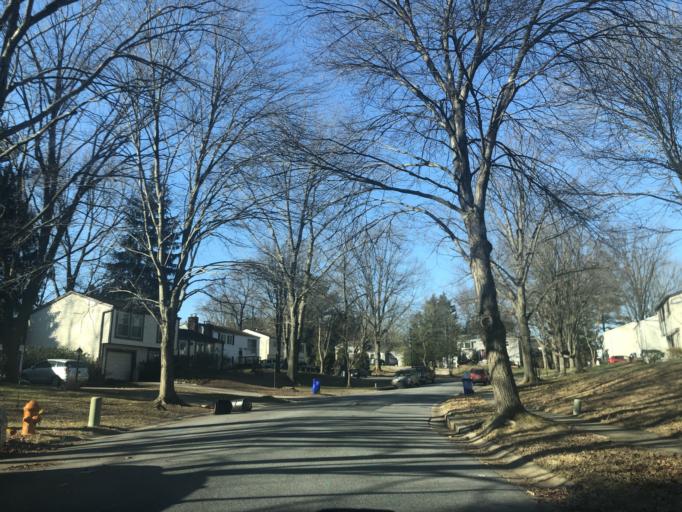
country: US
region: Maryland
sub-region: Howard County
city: Columbia
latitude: 39.2013
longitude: -76.8267
